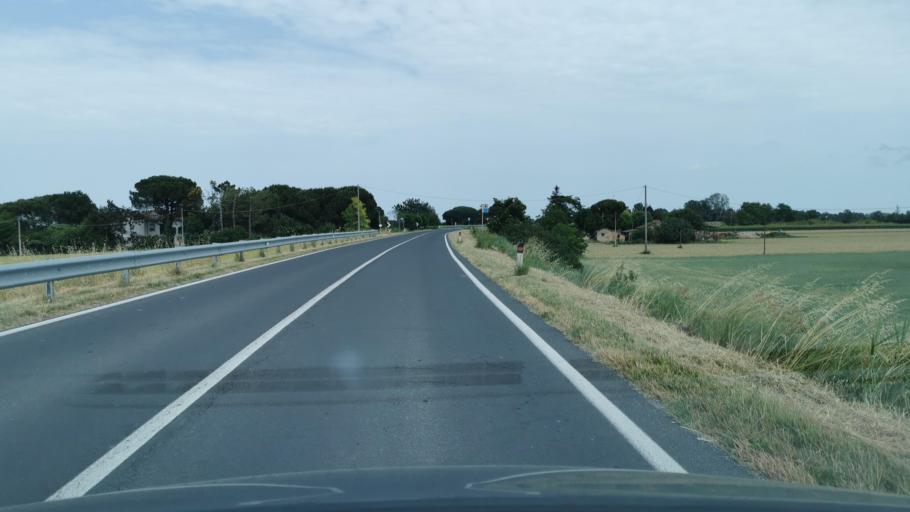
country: IT
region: Emilia-Romagna
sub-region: Provincia di Ravenna
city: Sant'Alberto
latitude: 44.5383
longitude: 12.1307
